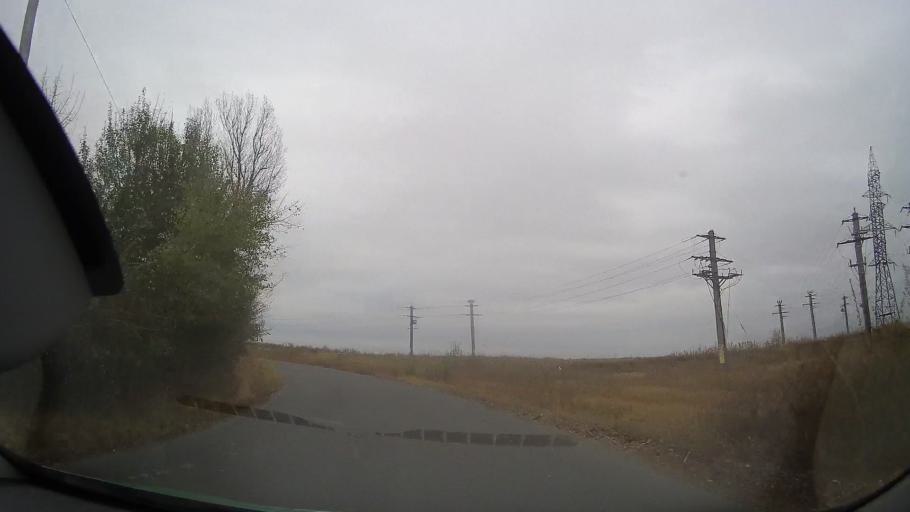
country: RO
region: Braila
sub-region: Comuna Rosiori
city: Rosiori
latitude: 44.8360
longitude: 27.3259
